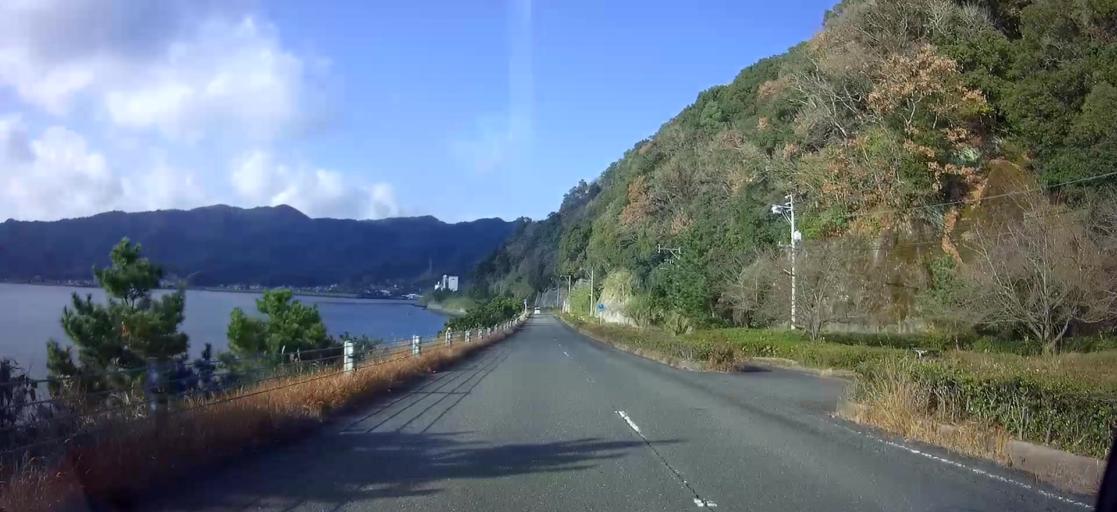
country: JP
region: Kumamoto
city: Minamata
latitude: 32.3838
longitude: 130.3794
